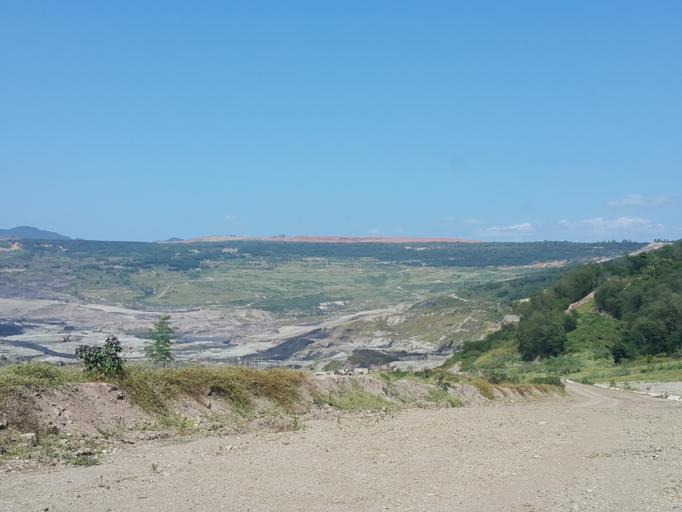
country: TH
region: Lampang
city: Mae Mo
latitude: 18.3218
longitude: 99.7369
